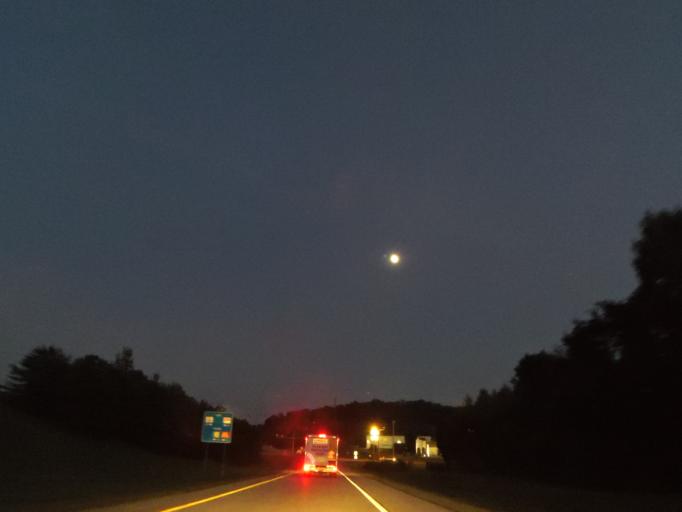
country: US
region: Tennessee
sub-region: Blount County
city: Louisville
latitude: 35.8468
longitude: -83.9954
